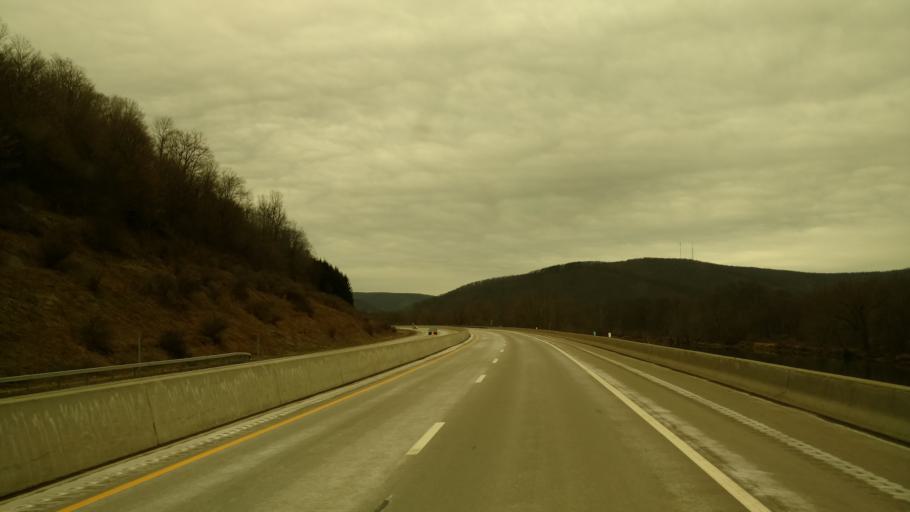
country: US
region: New York
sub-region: Cattaraugus County
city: Salamanca
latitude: 42.1407
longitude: -78.6660
